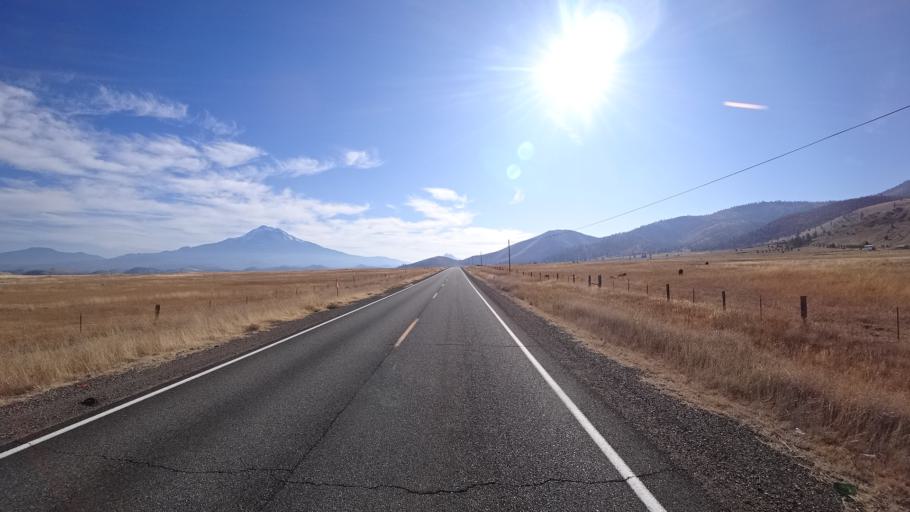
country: US
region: California
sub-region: Siskiyou County
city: Weed
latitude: 41.4854
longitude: -122.4999
